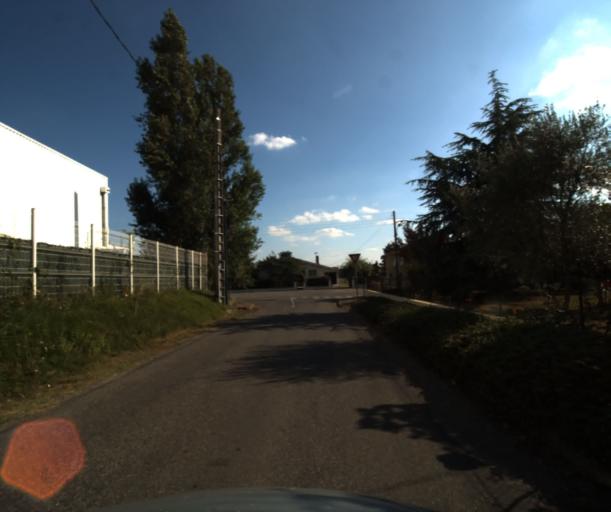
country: FR
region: Midi-Pyrenees
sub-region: Departement de la Haute-Garonne
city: Saint-Lys
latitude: 43.5122
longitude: 1.1877
